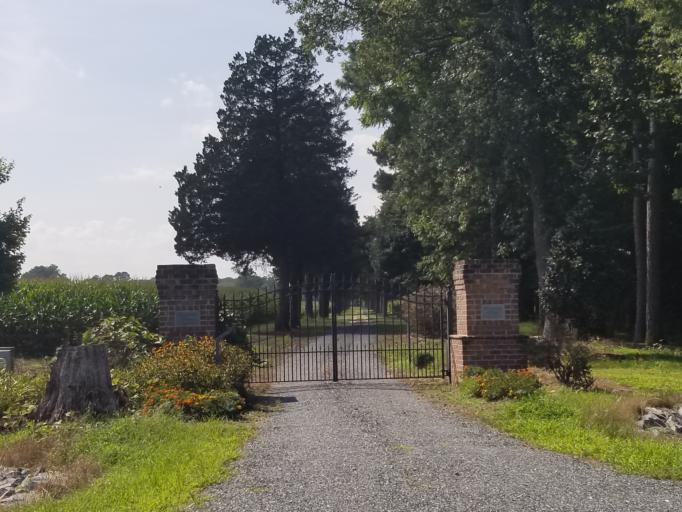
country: US
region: Maryland
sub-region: Somerset County
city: Princess Anne
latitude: 38.2617
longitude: -75.6817
